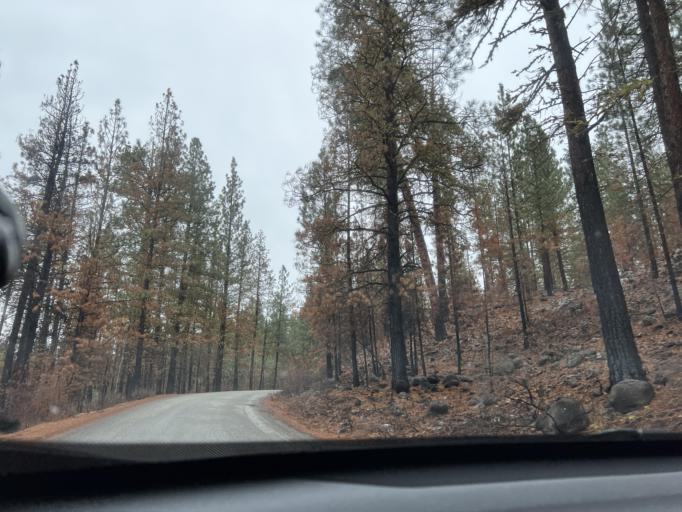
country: US
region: Washington
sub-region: Okanogan County
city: Brewster
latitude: 48.5749
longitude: -120.1702
